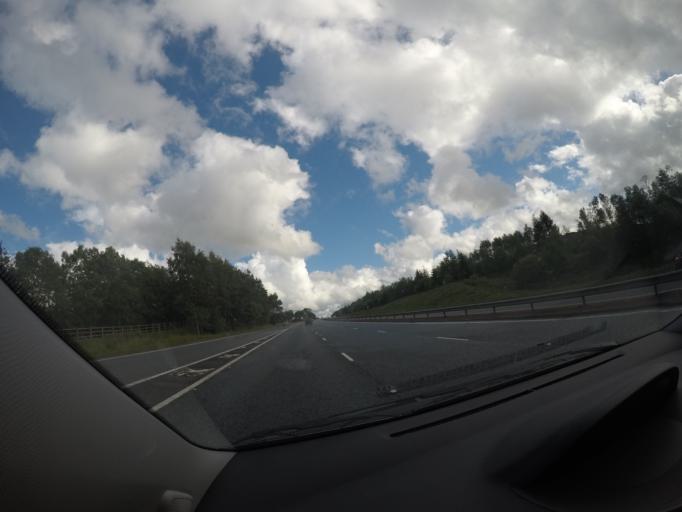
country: GB
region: Scotland
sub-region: South Lanarkshire
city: Douglas
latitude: 55.5721
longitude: -3.8103
